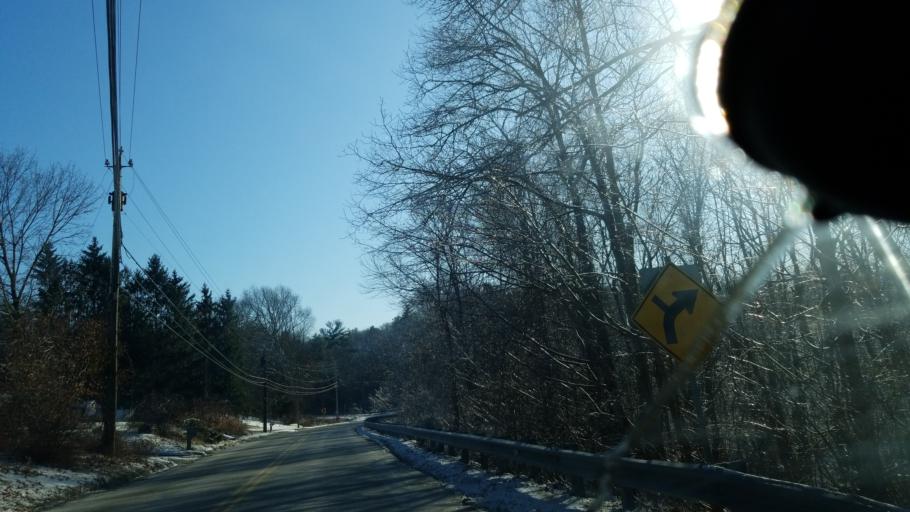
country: US
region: Connecticut
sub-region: Windham County
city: Danielson
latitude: 41.7897
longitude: -71.8796
